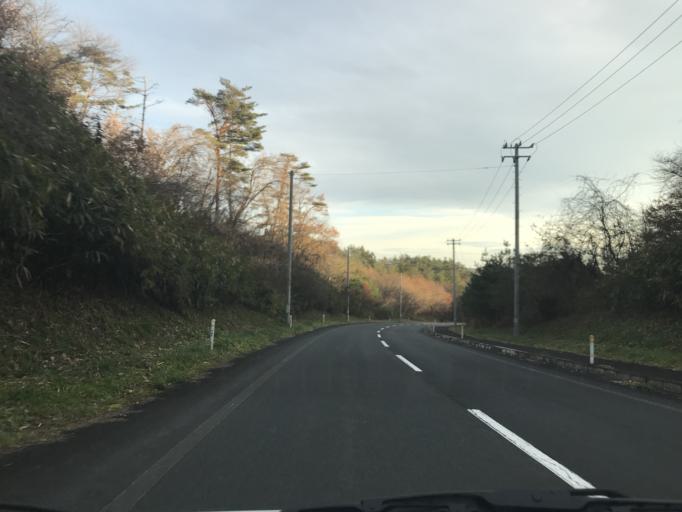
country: JP
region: Iwate
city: Ichinoseki
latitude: 38.9805
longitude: 141.0703
